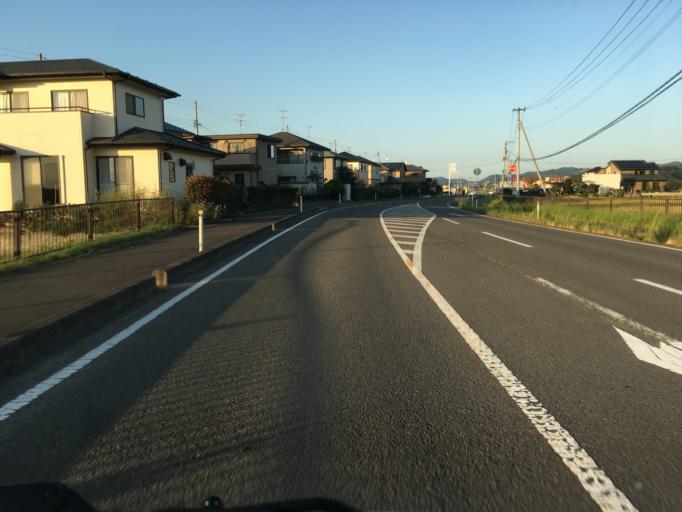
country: JP
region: Fukushima
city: Yanagawamachi-saiwaicho
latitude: 37.8348
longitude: 140.5951
